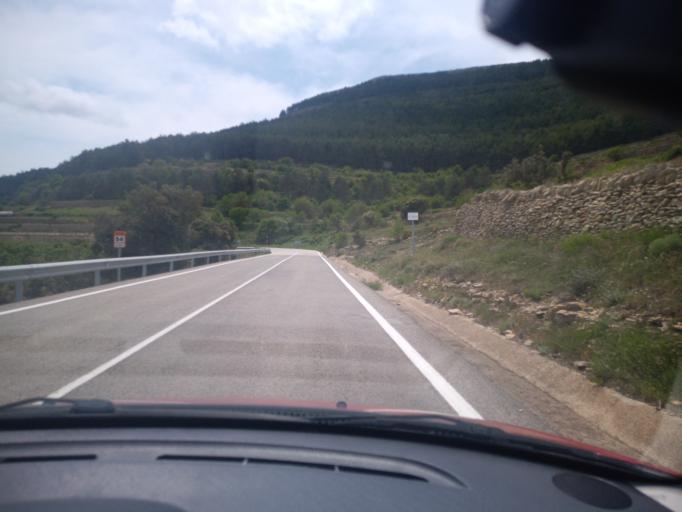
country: ES
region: Valencia
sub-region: Provincia de Castello
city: Ares del Maestre
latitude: 40.4589
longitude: -0.1490
